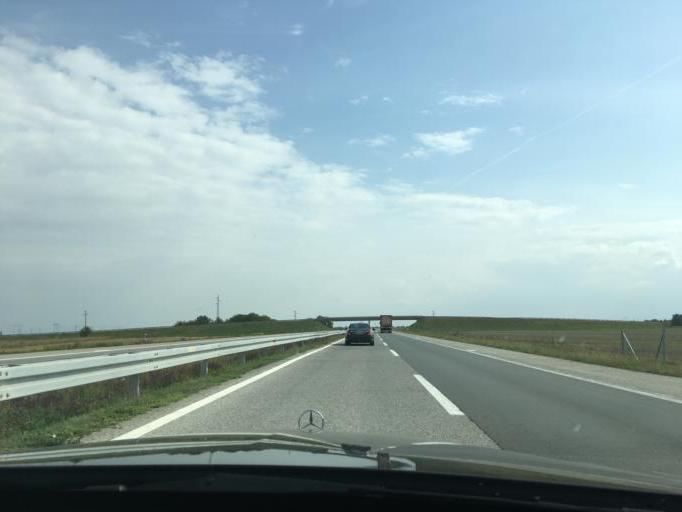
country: RS
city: Macvanska Mitrovica
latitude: 45.0143
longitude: 19.5728
